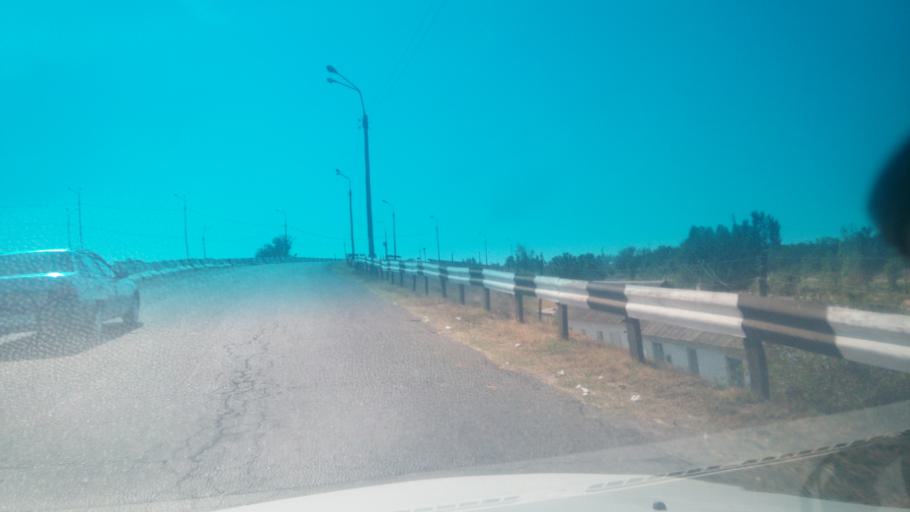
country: UZ
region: Sirdaryo
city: Sirdaryo
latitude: 40.8046
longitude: 68.6765
